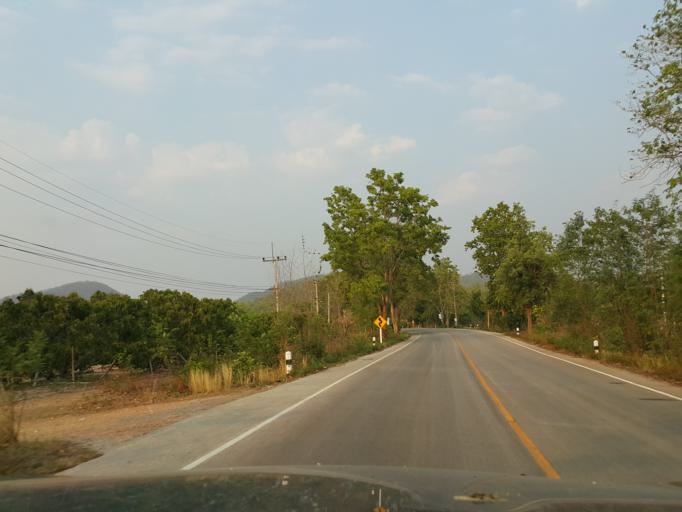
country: TH
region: Lamphun
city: Li
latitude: 17.8198
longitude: 98.9730
